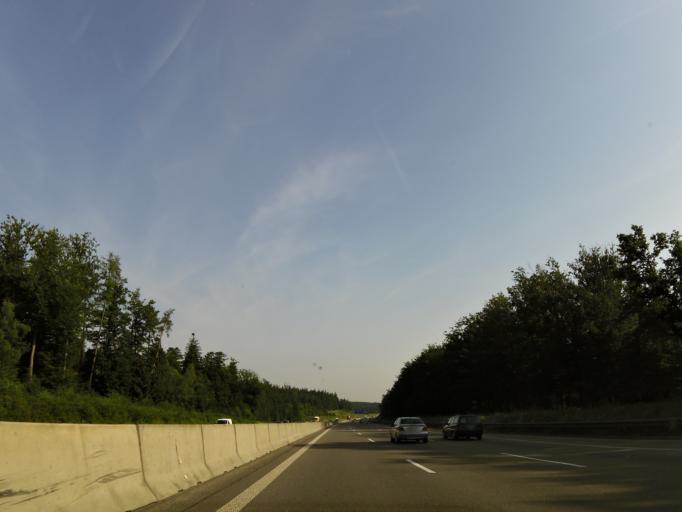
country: DE
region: Baden-Wuerttemberg
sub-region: Karlsruhe Region
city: Wurmberg
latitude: 48.8686
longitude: 8.7910
